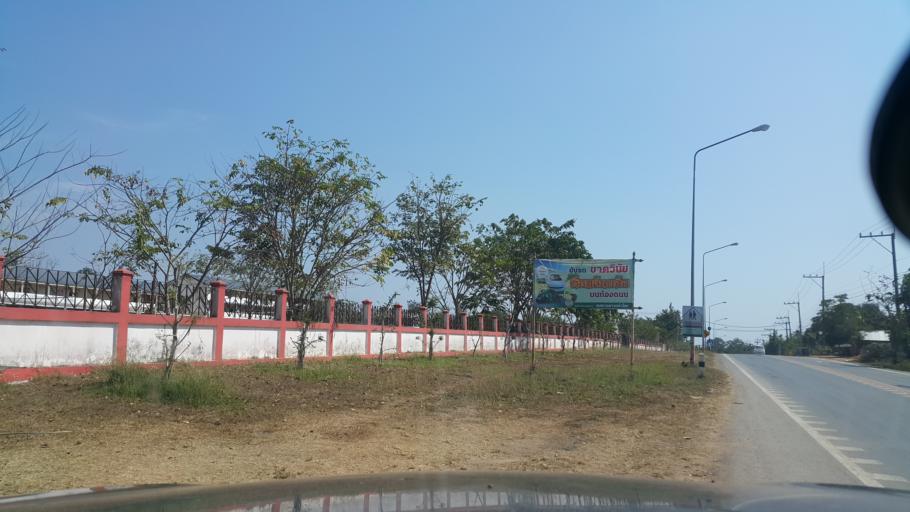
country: TH
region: Changwat Udon Thani
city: Nam Som
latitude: 17.7817
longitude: 102.1302
